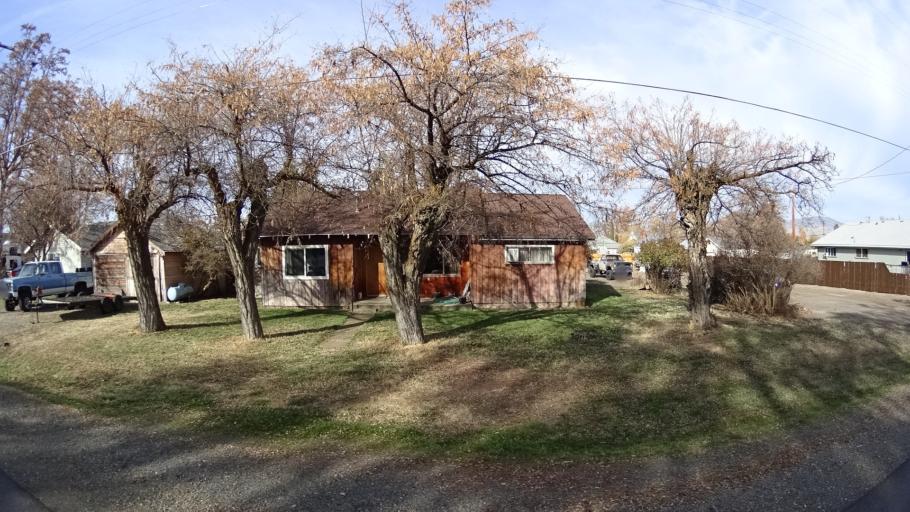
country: US
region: California
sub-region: Siskiyou County
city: Montague
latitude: 41.7272
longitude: -122.5229
